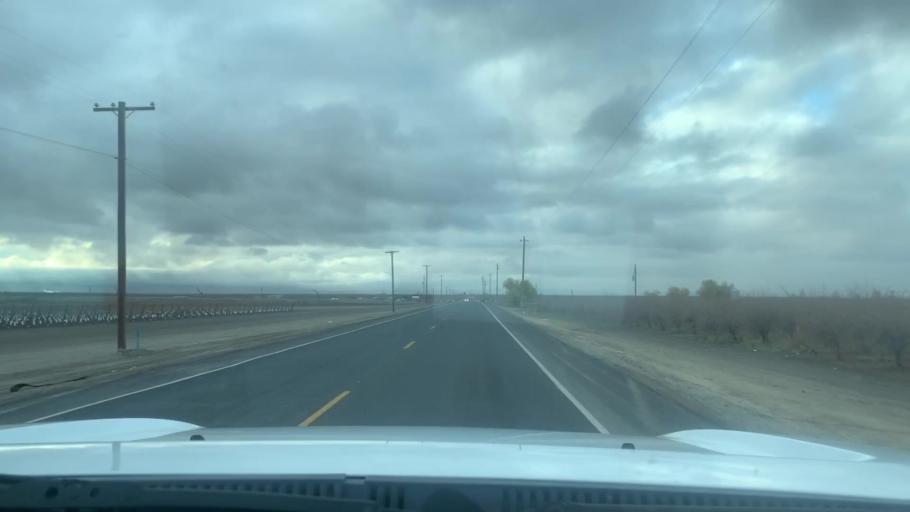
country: US
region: California
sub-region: Kern County
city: Lost Hills
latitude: 35.4995
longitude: -119.6152
